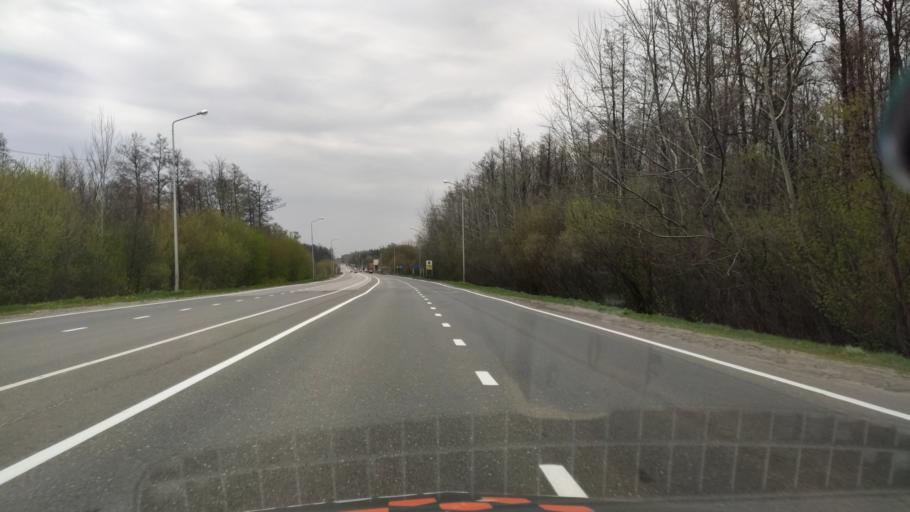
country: RU
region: Belgorod
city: Staryy Oskol
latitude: 51.3507
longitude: 37.8278
